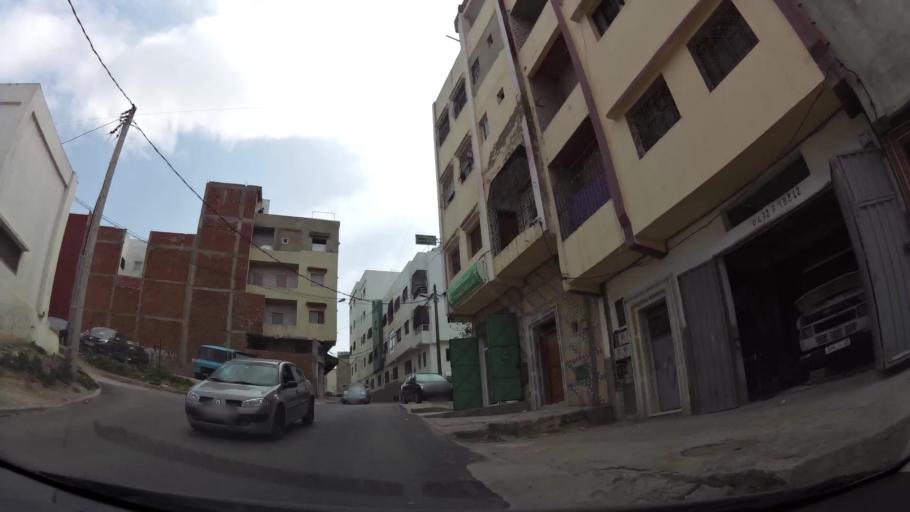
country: MA
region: Tanger-Tetouan
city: Tetouan
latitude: 35.5720
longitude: -5.3970
